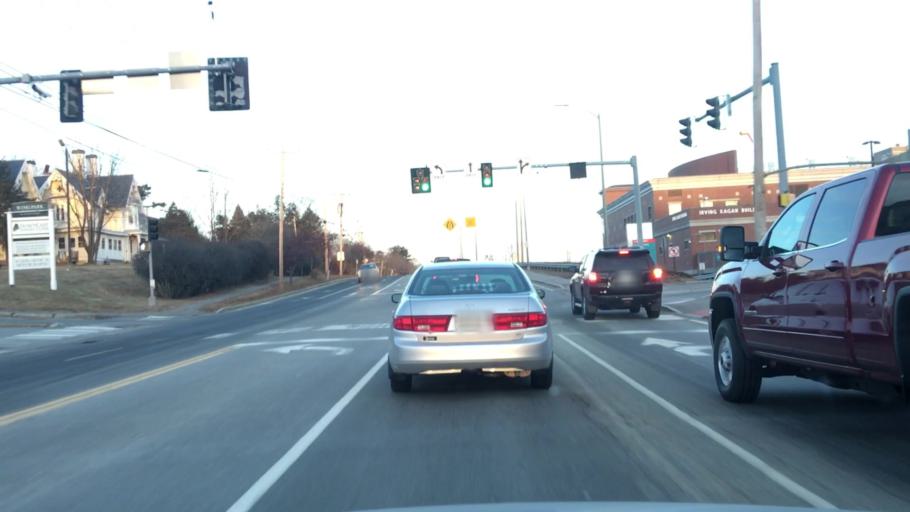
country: US
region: Maine
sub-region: Penobscot County
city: Brewer
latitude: 44.8082
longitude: -68.7538
